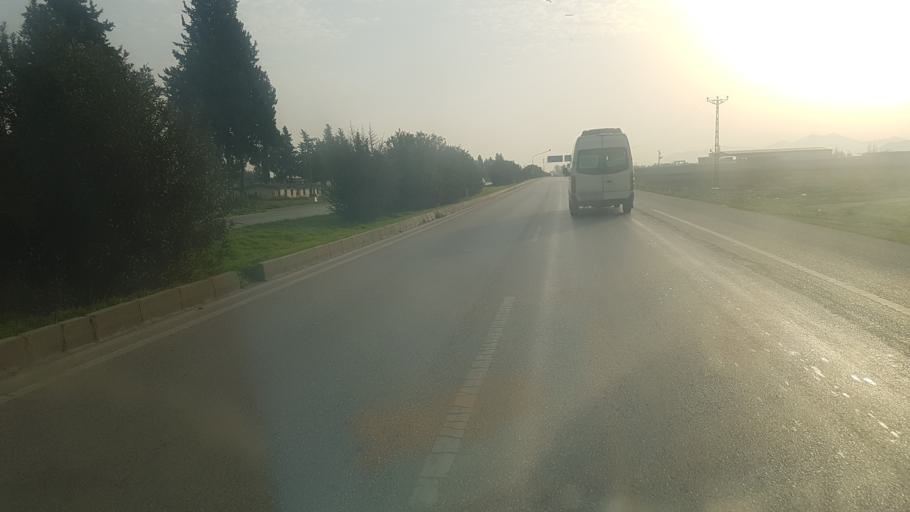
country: TR
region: Adana
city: Ceyhan
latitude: 37.0512
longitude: 35.8276
